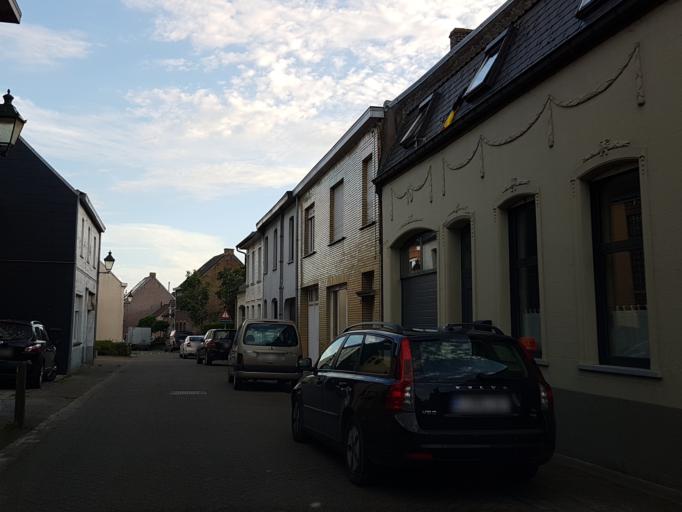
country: BE
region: Flanders
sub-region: Provincie Oost-Vlaanderen
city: Denderleeuw
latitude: 50.8976
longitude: 4.0439
